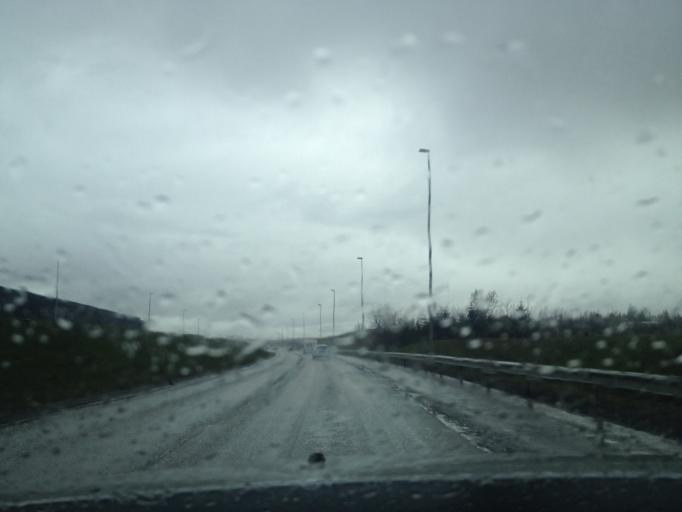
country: IS
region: Capital Region
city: Kopavogur
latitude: 64.0909
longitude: -21.8920
